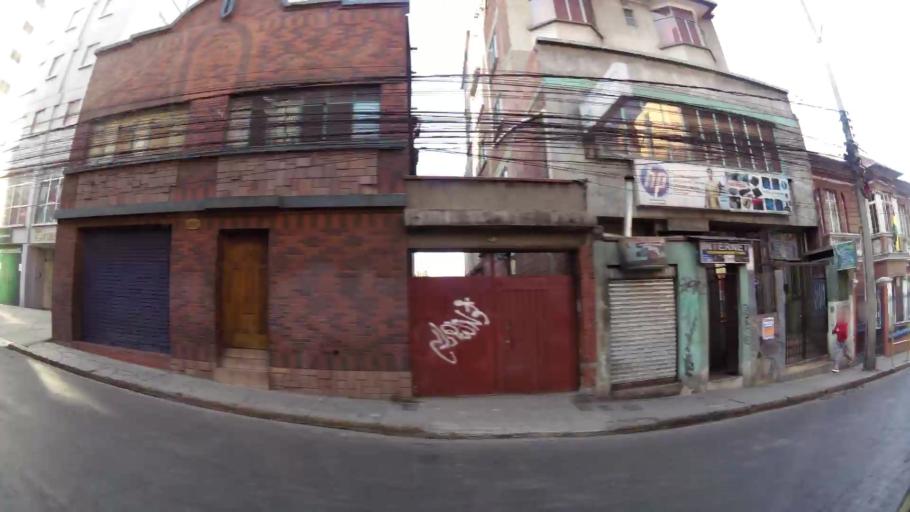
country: BO
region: La Paz
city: La Paz
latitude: -16.5036
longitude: -68.1291
